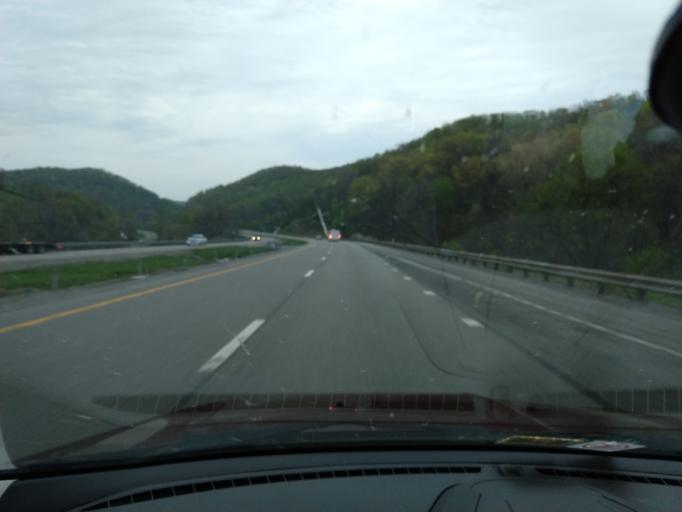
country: US
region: West Virginia
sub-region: Lewis County
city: Weston
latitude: 38.9689
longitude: -80.5132
